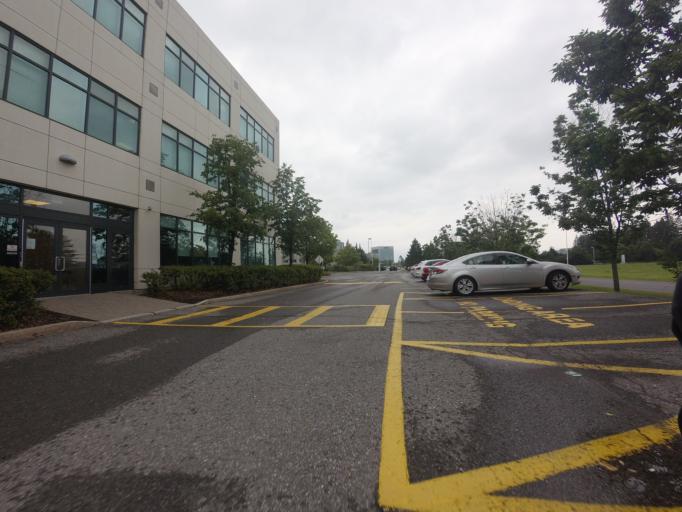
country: CA
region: Ontario
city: Bells Corners
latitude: 45.3430
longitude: -75.9227
